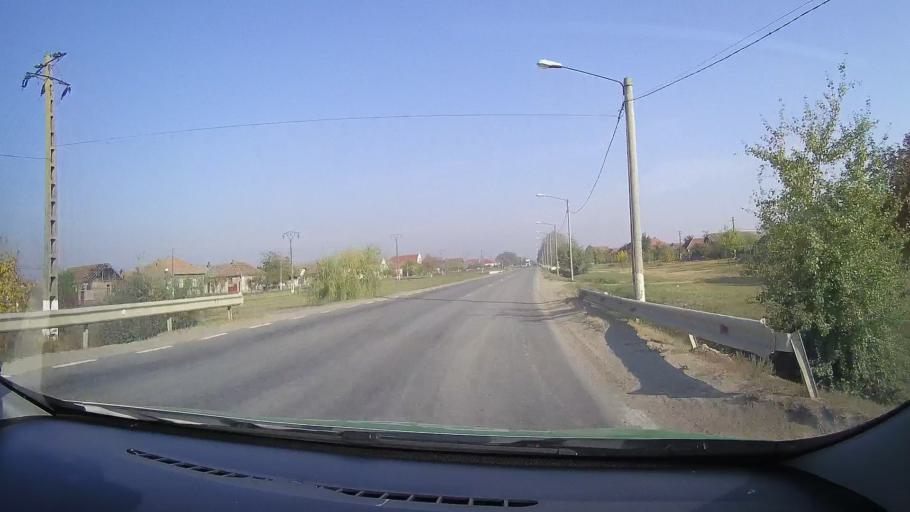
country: RO
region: Arad
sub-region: Comuna Pilu
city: Pilu
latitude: 46.5714
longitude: 21.3420
